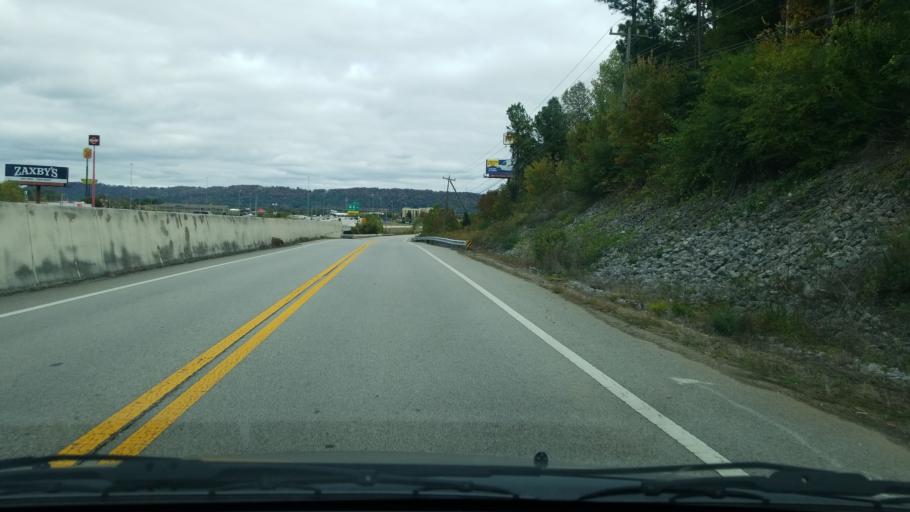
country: US
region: Tennessee
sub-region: Hamilton County
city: Collegedale
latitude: 35.0838
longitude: -85.0740
